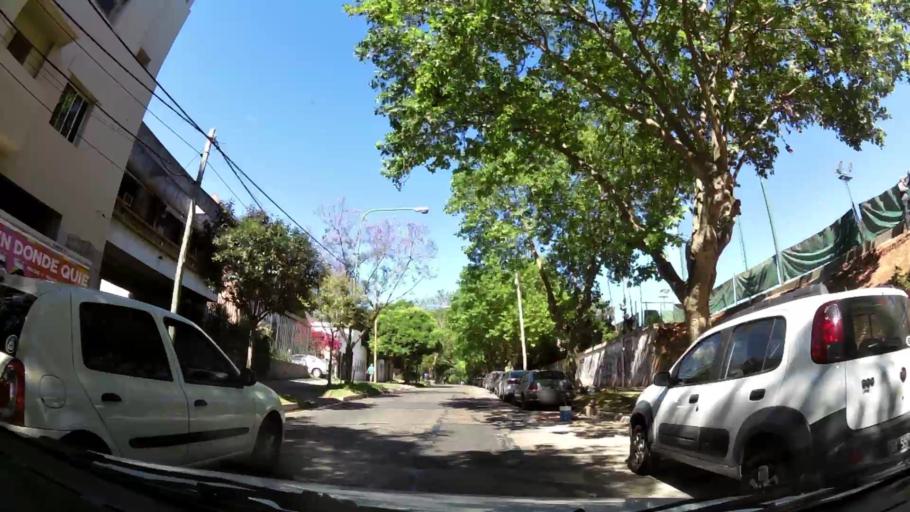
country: AR
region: Buenos Aires
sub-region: Partido de Vicente Lopez
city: Olivos
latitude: -34.5177
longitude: -58.4788
